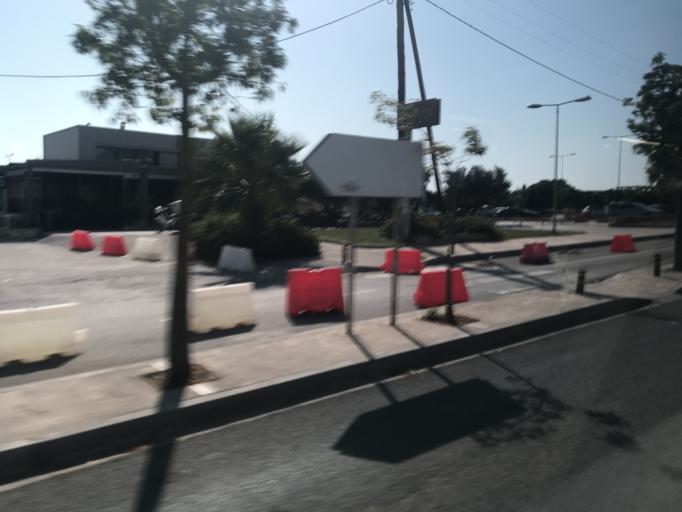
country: GR
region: Crete
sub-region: Nomos Irakleiou
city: Gazi
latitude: 35.3044
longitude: 25.0854
